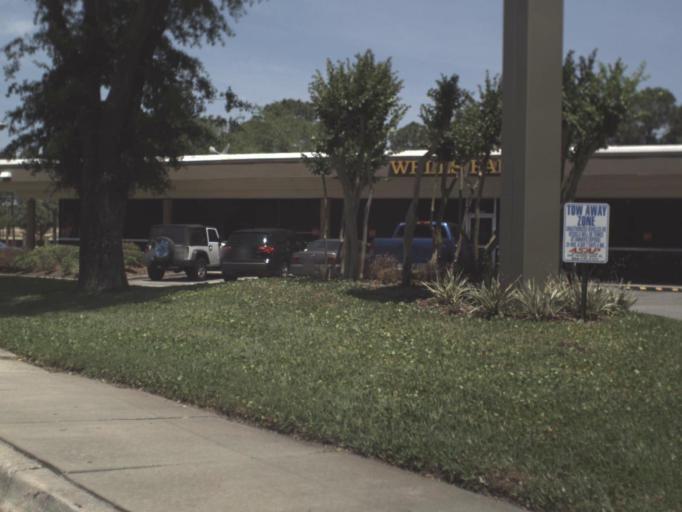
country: US
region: Florida
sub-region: Saint Johns County
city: Fruit Cove
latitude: 30.2202
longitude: -81.5577
